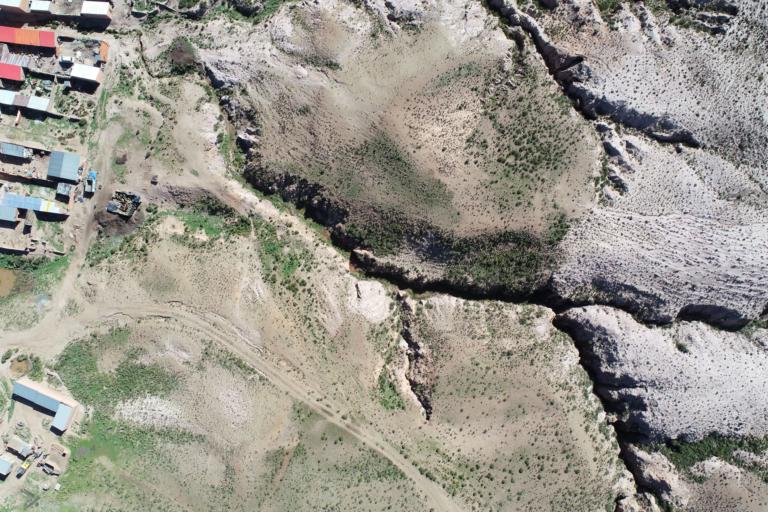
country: BO
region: La Paz
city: Patacamaya
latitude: -17.3023
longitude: -68.4833
